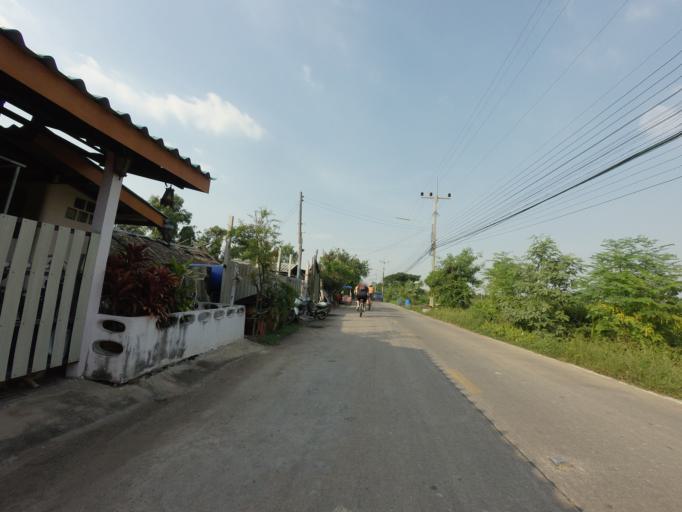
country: TH
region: Samut Sakhon
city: Samut Sakhon
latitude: 13.5093
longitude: 100.3069
